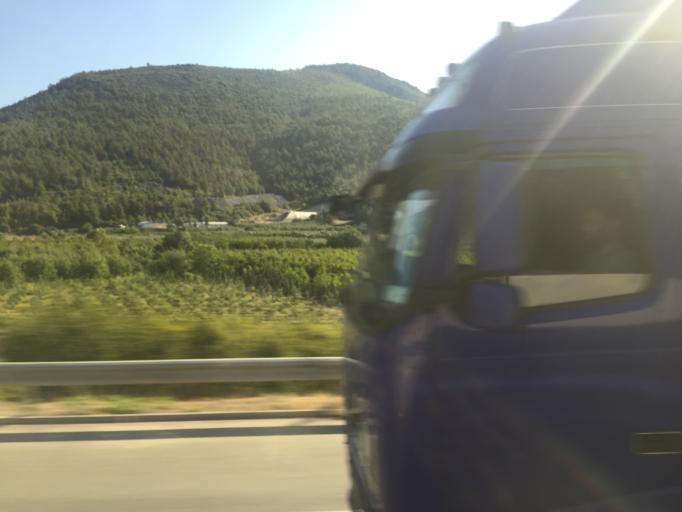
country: TR
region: Bursa
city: Kestel
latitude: 40.2372
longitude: 29.2645
